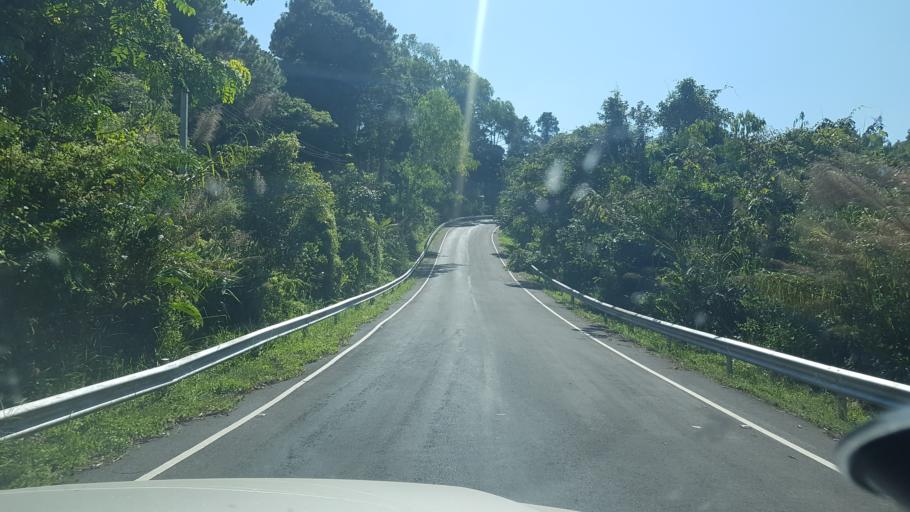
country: TH
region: Phetchabun
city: Khao Kho
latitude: 16.5544
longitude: 100.9812
